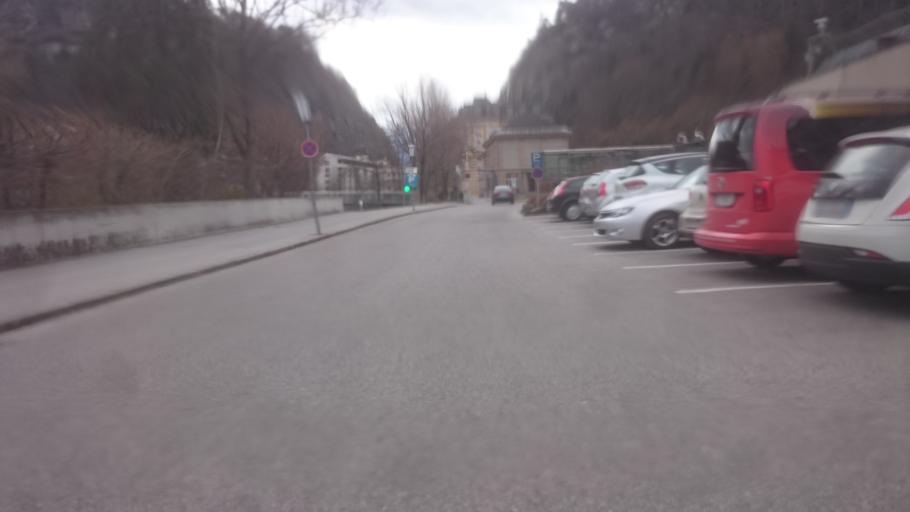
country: AT
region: Vorarlberg
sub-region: Politischer Bezirk Feldkirch
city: Feldkirch
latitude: 47.2364
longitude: 9.5938
